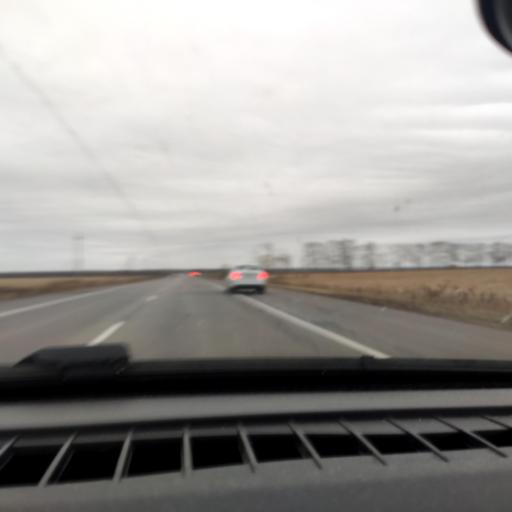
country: RU
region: Voronezj
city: Strelitsa
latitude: 51.5346
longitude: 38.9695
